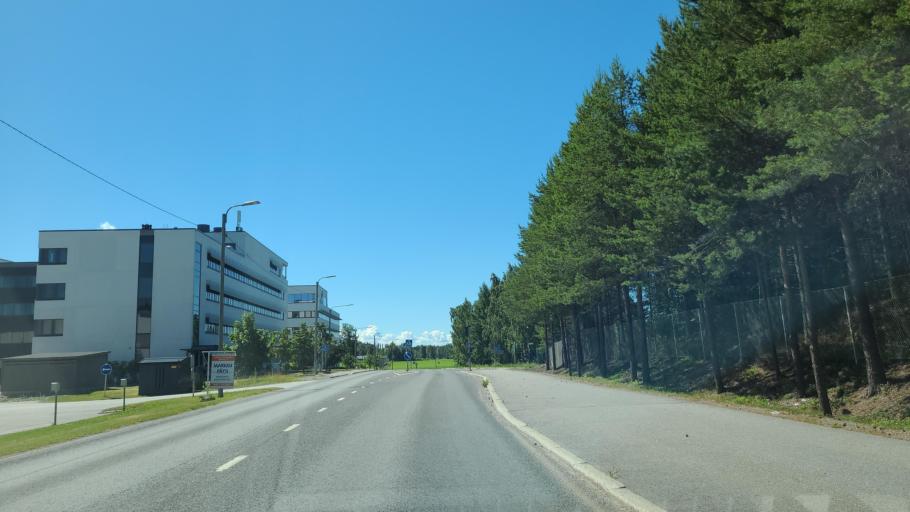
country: FI
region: Ostrobothnia
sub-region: Vaasa
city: Ristinummi
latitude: 63.0583
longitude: 21.7322
